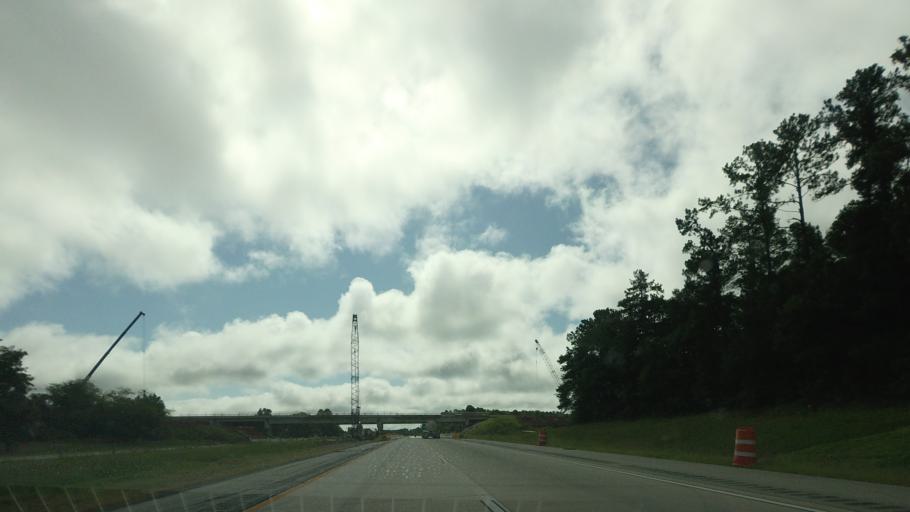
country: US
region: Georgia
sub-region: Twiggs County
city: Jeffersonville
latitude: 32.6244
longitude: -83.3715
